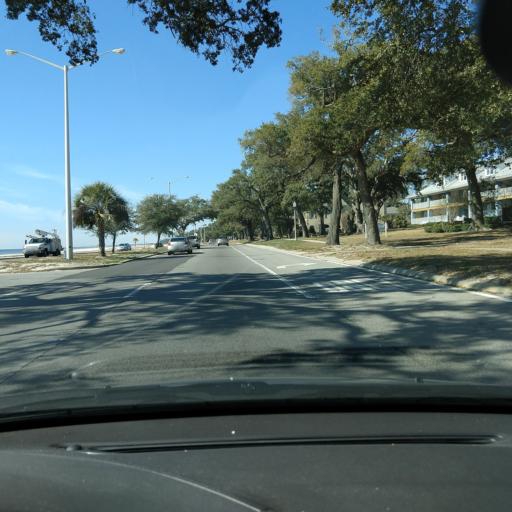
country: US
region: Mississippi
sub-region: Harrison County
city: Biloxi
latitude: 30.3948
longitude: -88.9127
